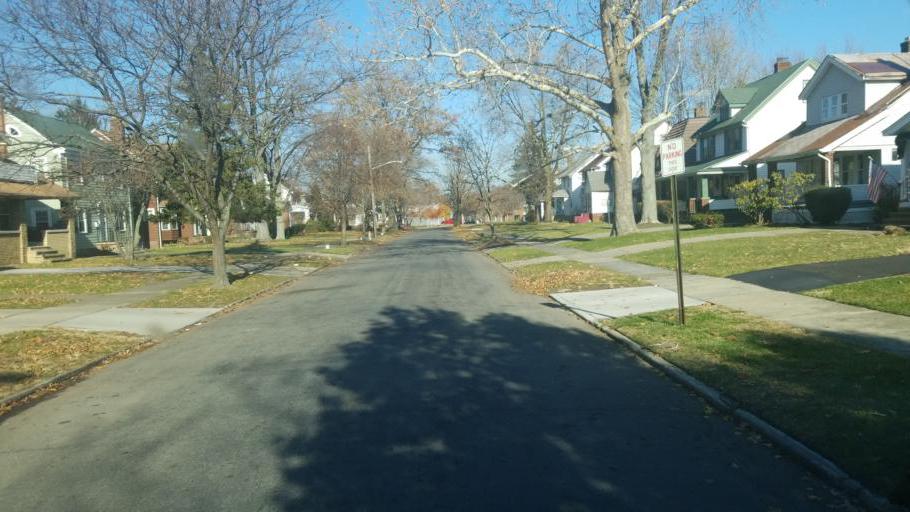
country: US
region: Ohio
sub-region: Cuyahoga County
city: Cleveland Heights
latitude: 41.5331
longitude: -81.5510
